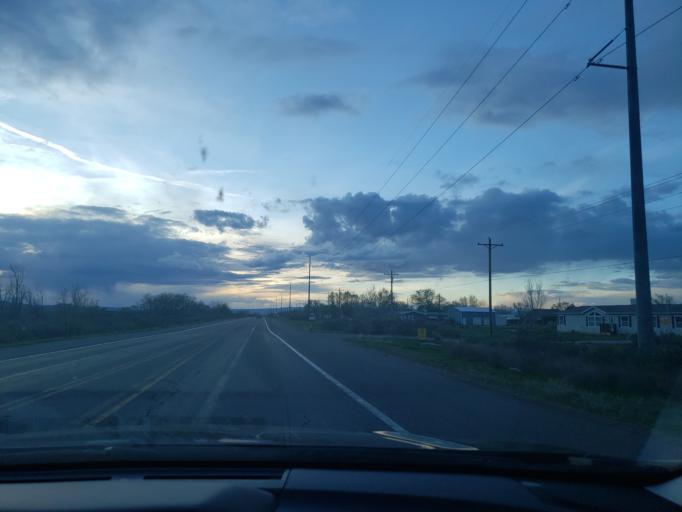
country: US
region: Colorado
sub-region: Mesa County
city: Redlands
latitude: 39.1251
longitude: -108.6741
